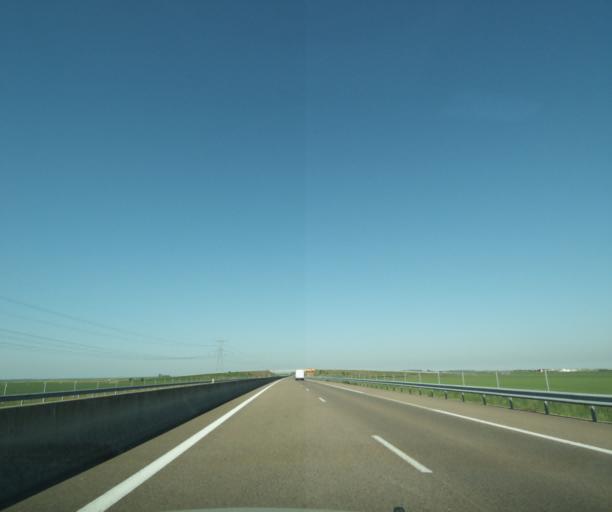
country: FR
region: Centre
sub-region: Departement du Loiret
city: Boynes
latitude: 48.0965
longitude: 2.3732
